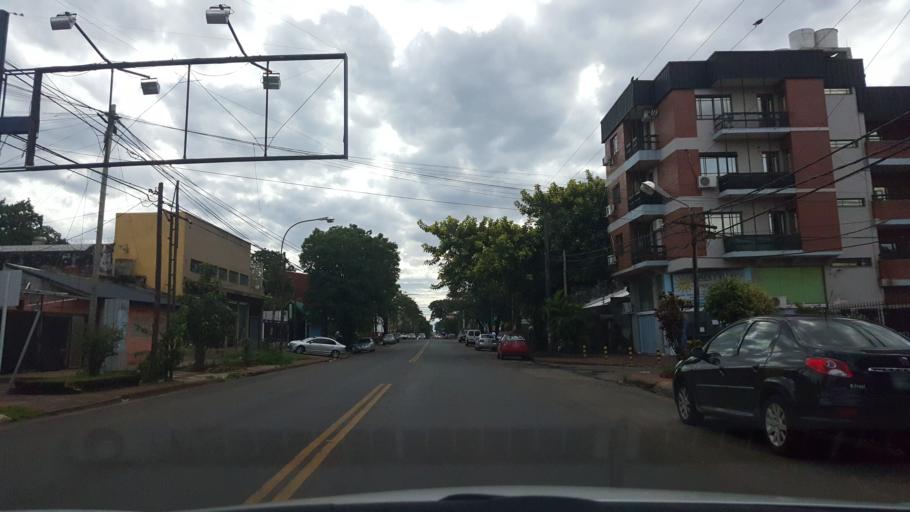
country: AR
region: Misiones
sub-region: Departamento de Capital
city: Posadas
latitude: -27.3732
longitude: -55.9083
